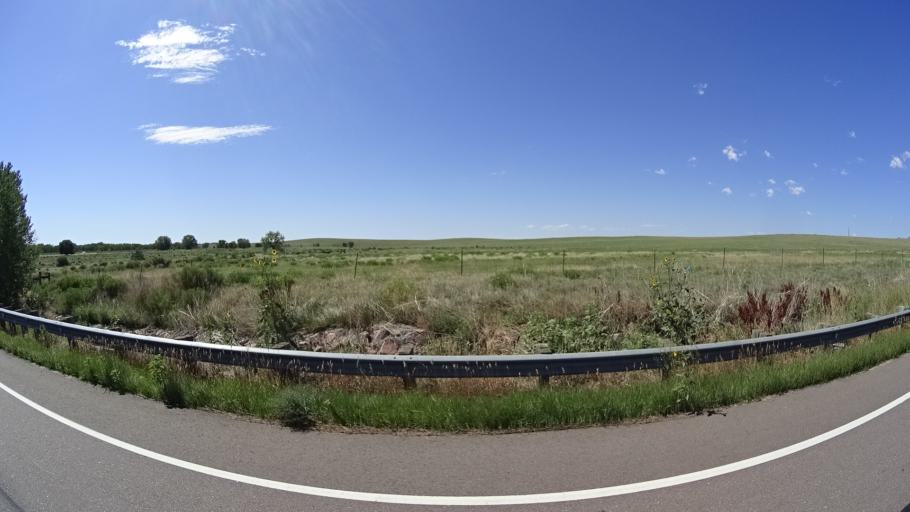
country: US
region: Colorado
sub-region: El Paso County
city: Security-Widefield
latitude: 38.7622
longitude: -104.6627
